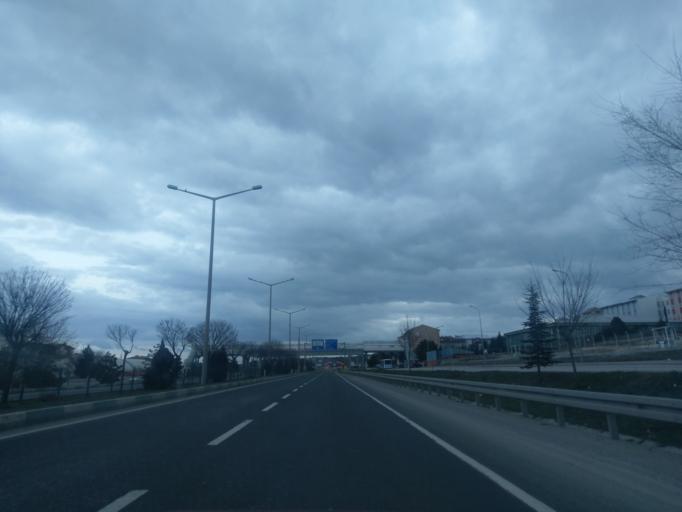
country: TR
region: Kuetahya
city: Kutahya
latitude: 39.3867
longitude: 30.0404
